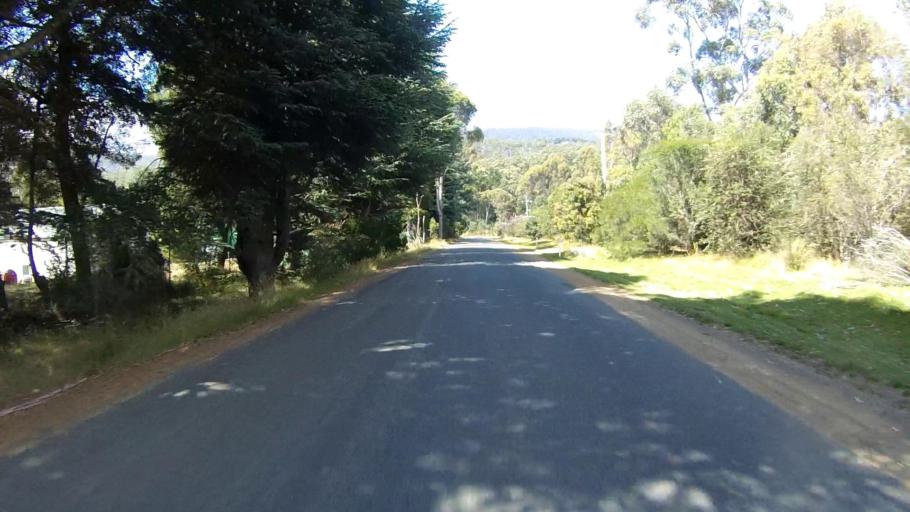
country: AU
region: Tasmania
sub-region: Derwent Valley
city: New Norfolk
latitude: -42.6834
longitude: 146.7202
